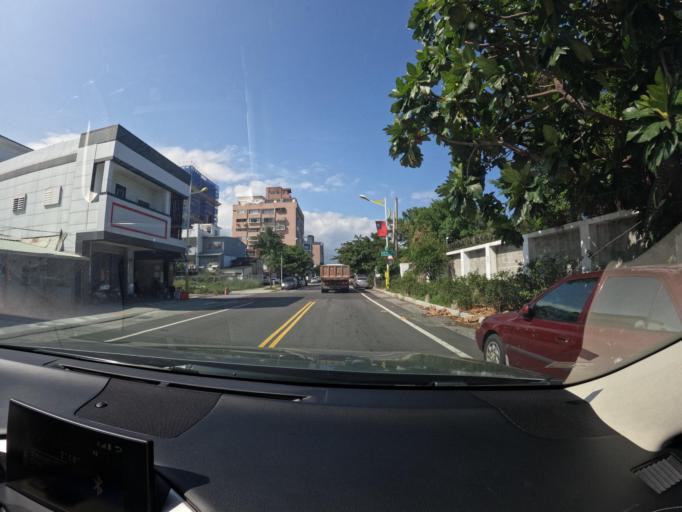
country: TW
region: Taiwan
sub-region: Hualien
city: Hualian
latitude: 23.9915
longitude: 121.6340
